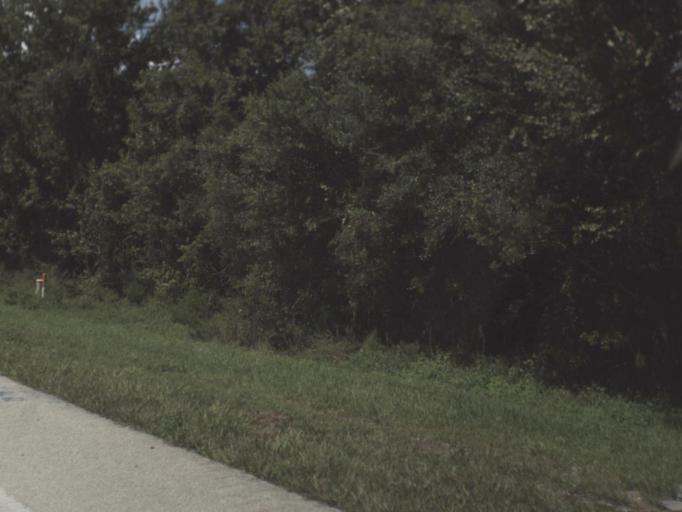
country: US
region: Florida
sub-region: DeSoto County
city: Nocatee
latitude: 27.1058
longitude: -81.9321
